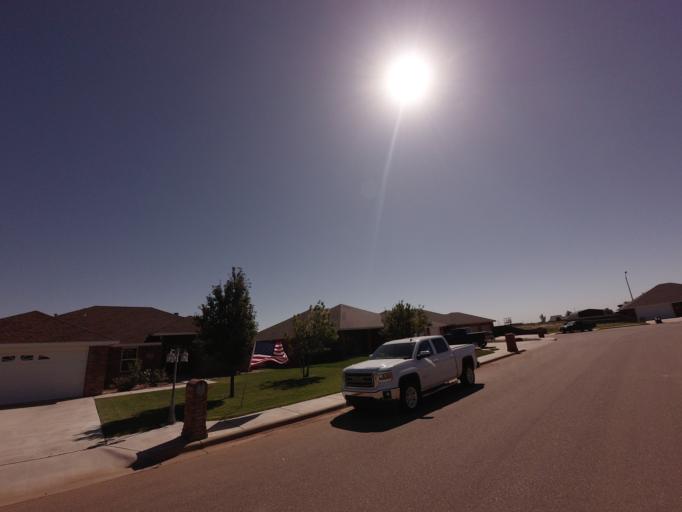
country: US
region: New Mexico
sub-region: Curry County
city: Clovis
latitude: 34.4222
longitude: -103.1570
